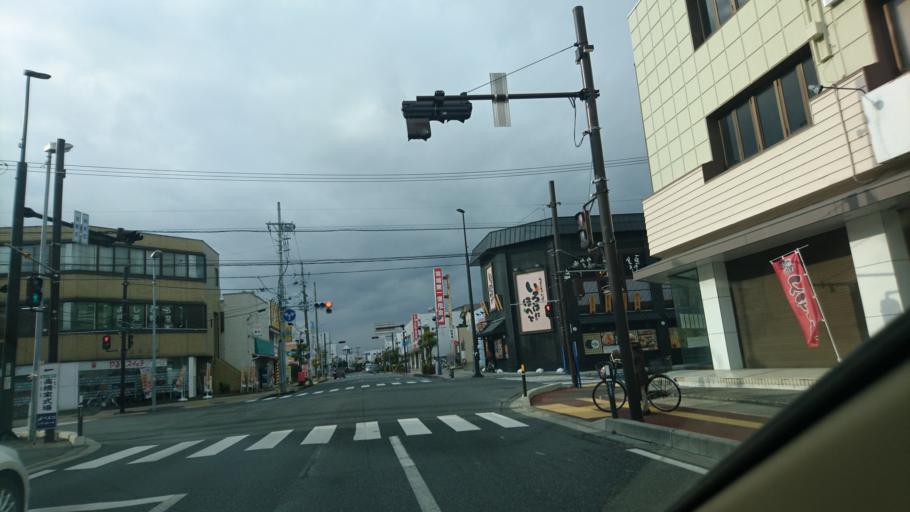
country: JP
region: Miyagi
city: Furukawa
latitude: 38.5736
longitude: 140.9650
